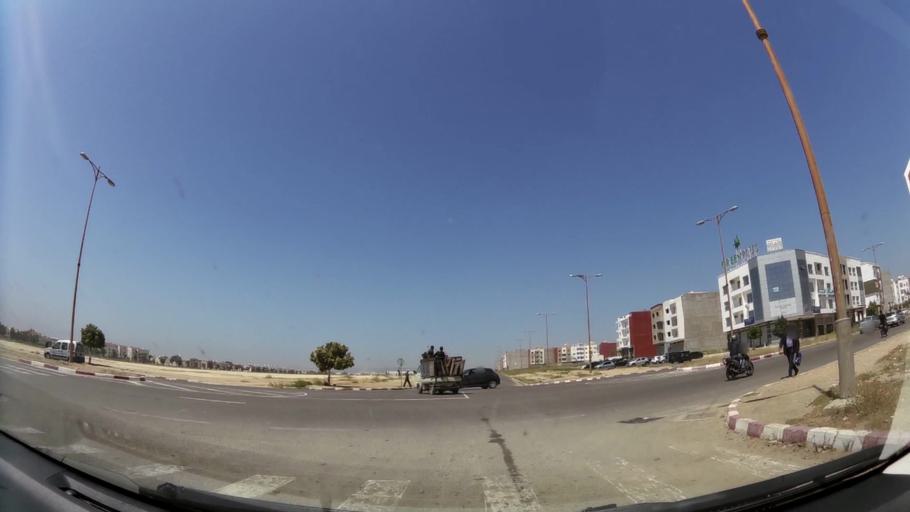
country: MA
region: Oued ed Dahab-Lagouira
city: Dakhla
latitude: 30.4265
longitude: -9.5564
